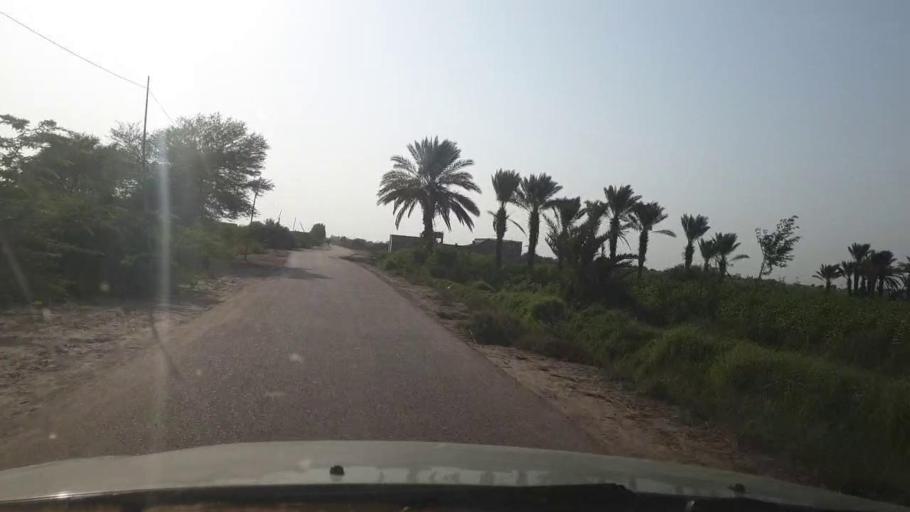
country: PK
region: Sindh
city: Tando Ghulam Ali
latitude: 25.1834
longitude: 68.9477
